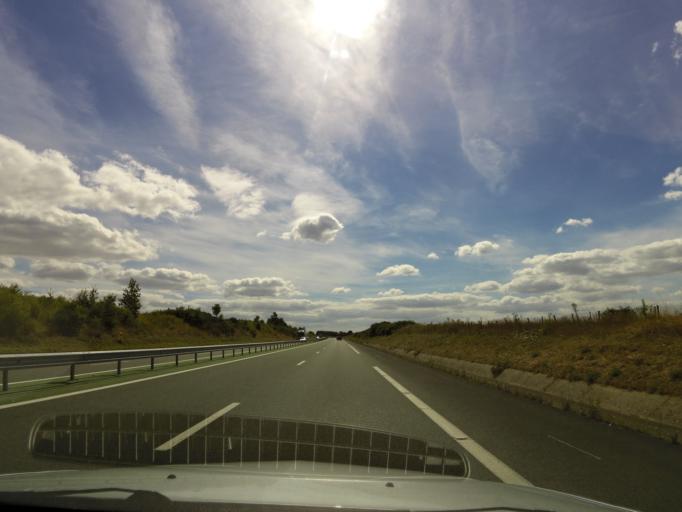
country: FR
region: Pays de la Loire
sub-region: Departement de la Vendee
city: Les Essarts
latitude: 46.7772
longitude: -1.2606
